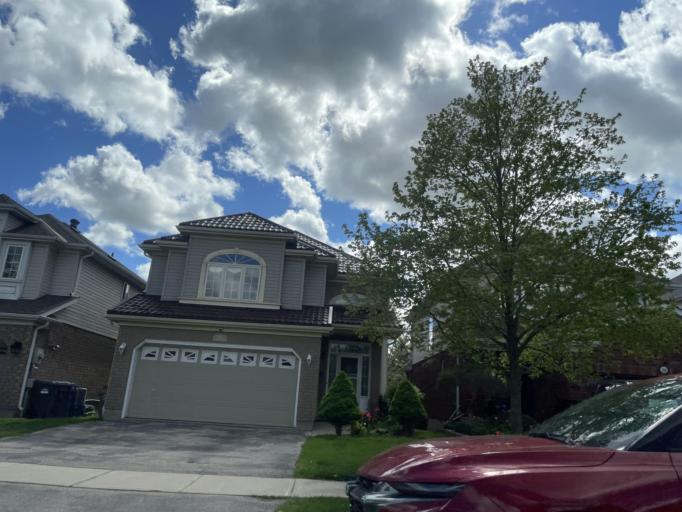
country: CA
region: Ontario
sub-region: Wellington County
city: Guelph
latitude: 43.5046
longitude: -80.1908
